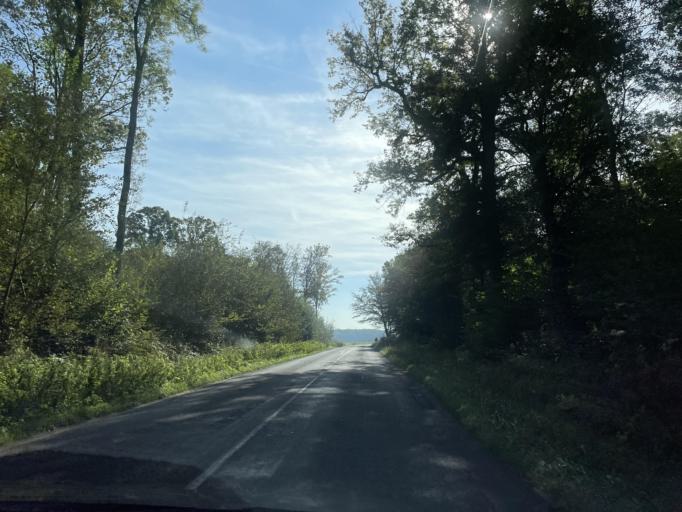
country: FR
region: Ile-de-France
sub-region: Departement de Seine-et-Marne
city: Sammeron
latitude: 48.8936
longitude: 3.0638
